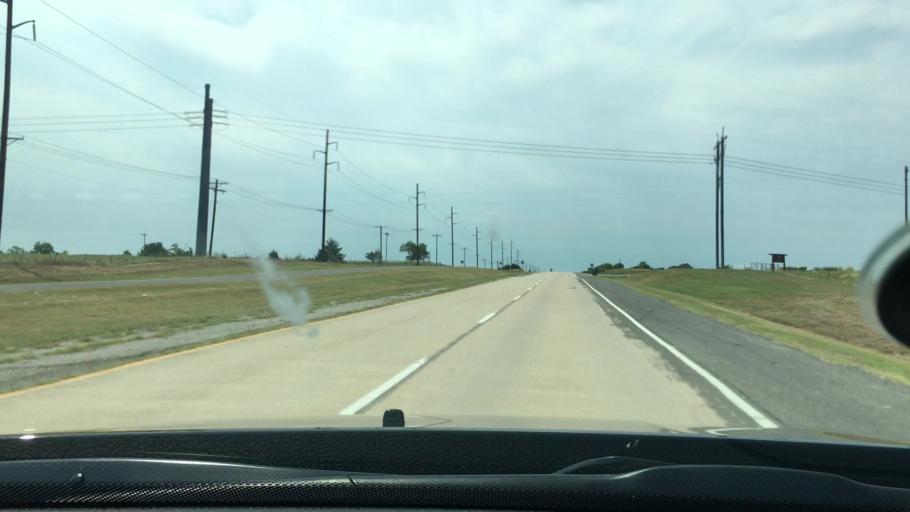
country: US
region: Oklahoma
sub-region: Carter County
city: Ardmore
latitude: 34.2334
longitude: -97.1432
